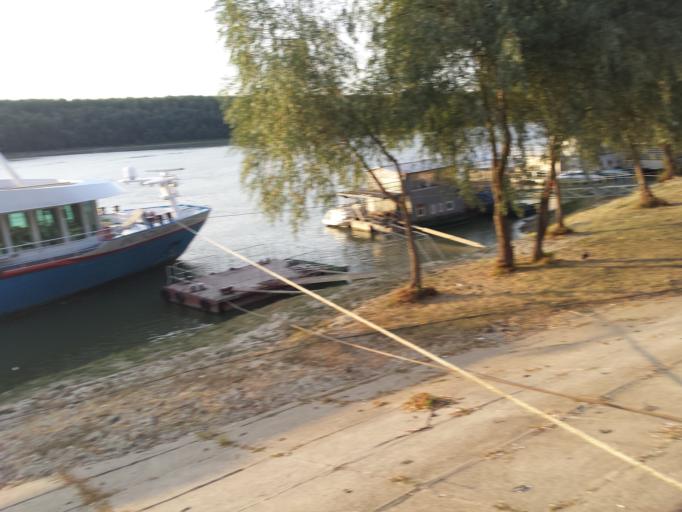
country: RO
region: Braila
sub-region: Municipiul Braila
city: Braila
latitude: 45.2694
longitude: 27.9809
